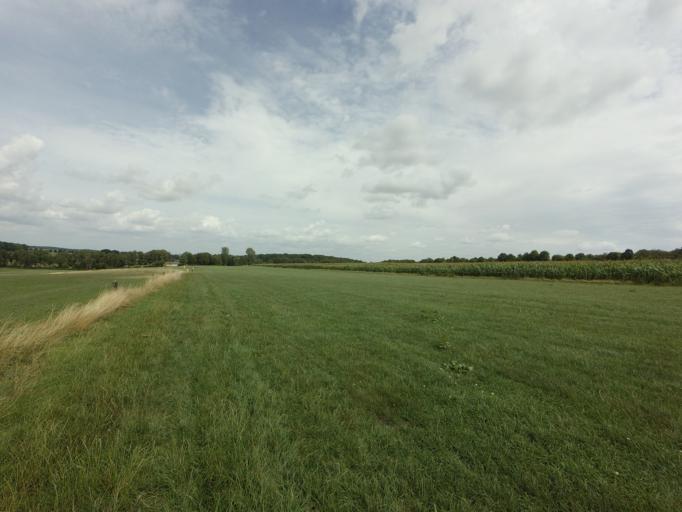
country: NL
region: Limburg
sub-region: Valkenburg aan de Geul
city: Schin op Geul
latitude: 50.7888
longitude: 5.8864
